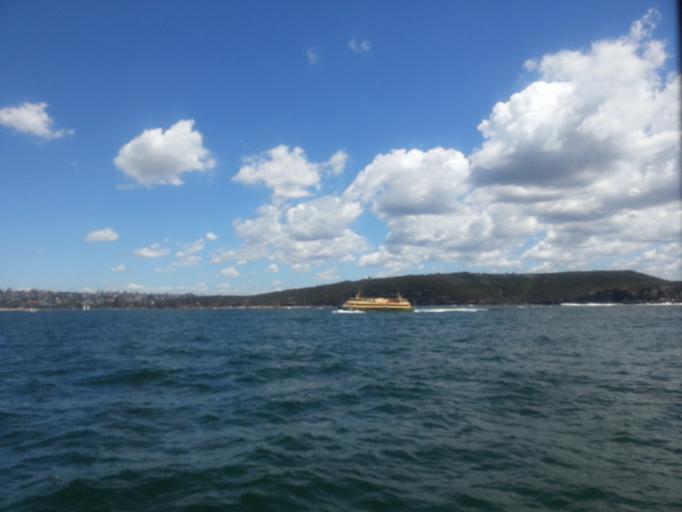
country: AU
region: New South Wales
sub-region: Manly Vale
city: Manly
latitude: -33.8211
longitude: 151.2792
